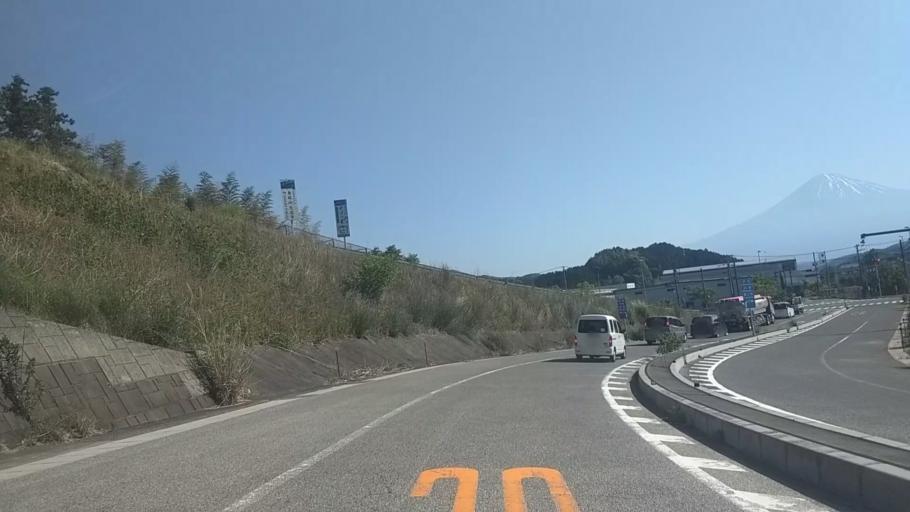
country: JP
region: Shizuoka
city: Fujinomiya
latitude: 35.1503
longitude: 138.5201
